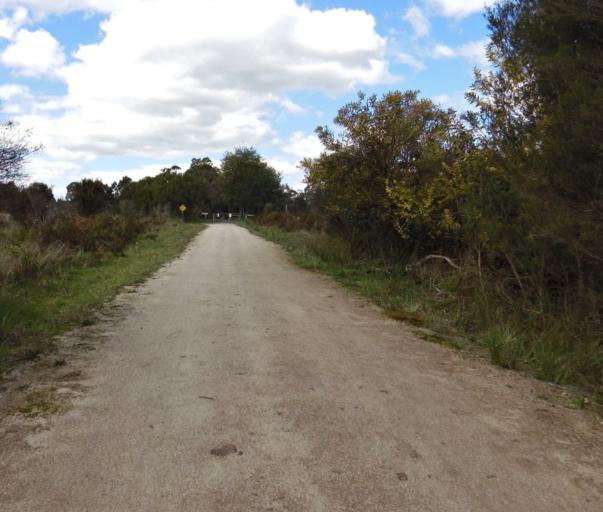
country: AU
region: Victoria
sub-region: Bass Coast
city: North Wonthaggi
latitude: -38.5856
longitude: 146.0366
